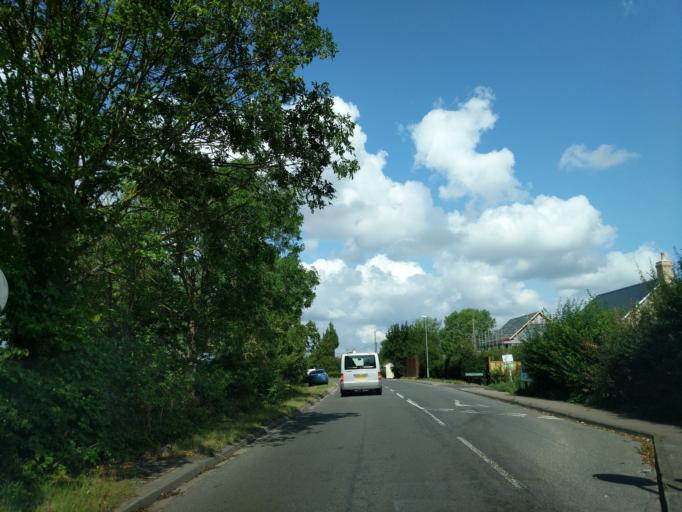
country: GB
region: England
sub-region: Cambridgeshire
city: Isleham
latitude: 52.3113
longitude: 0.3806
